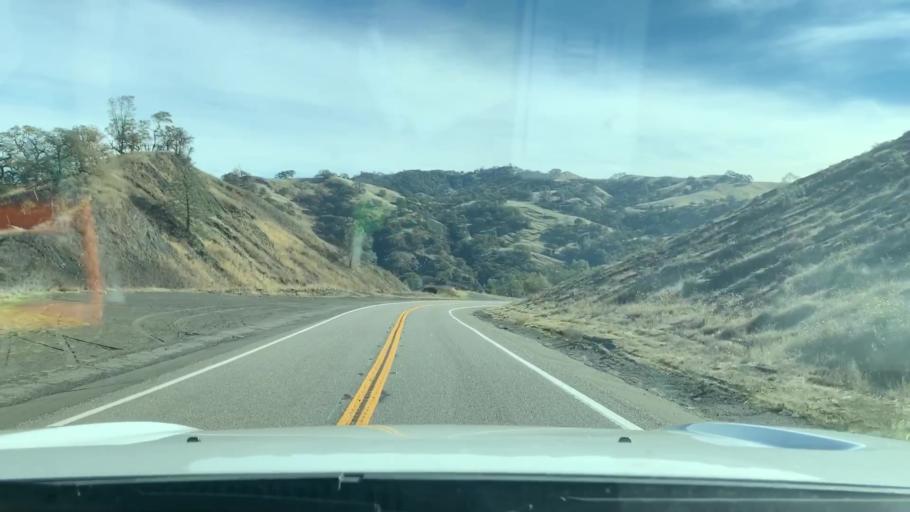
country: US
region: California
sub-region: Monterey County
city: King City
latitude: 36.1907
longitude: -120.7550
